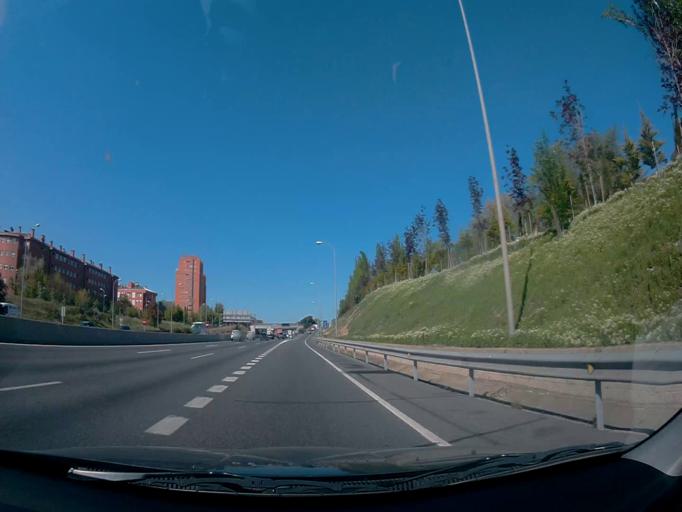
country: ES
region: Madrid
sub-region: Provincia de Madrid
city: Vicalvaro
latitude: 40.4030
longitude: -3.6254
